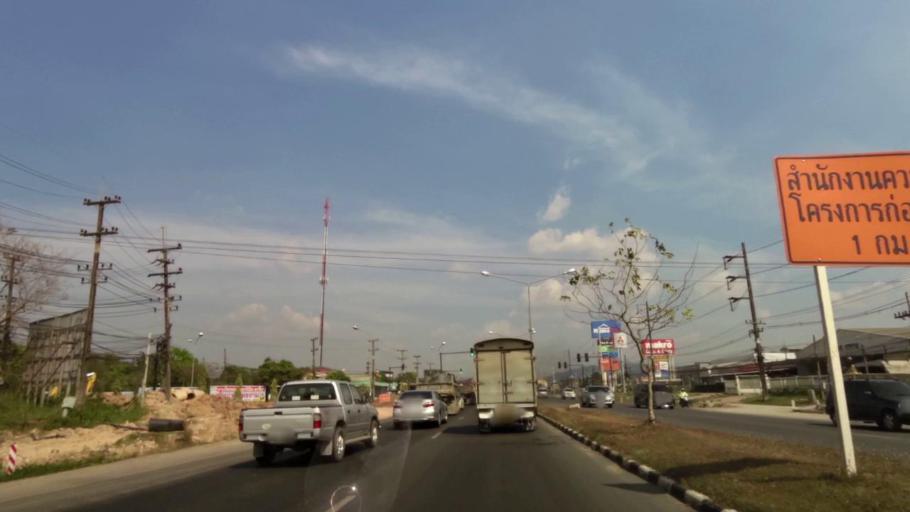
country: TH
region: Chanthaburi
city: Chanthaburi
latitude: 12.6160
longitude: 102.1409
